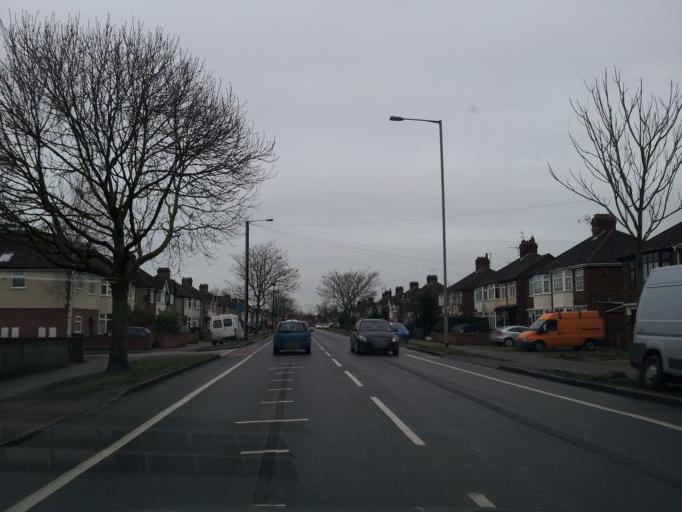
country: GB
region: England
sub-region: Cambridgeshire
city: Cambridge
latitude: 52.1896
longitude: 0.1536
